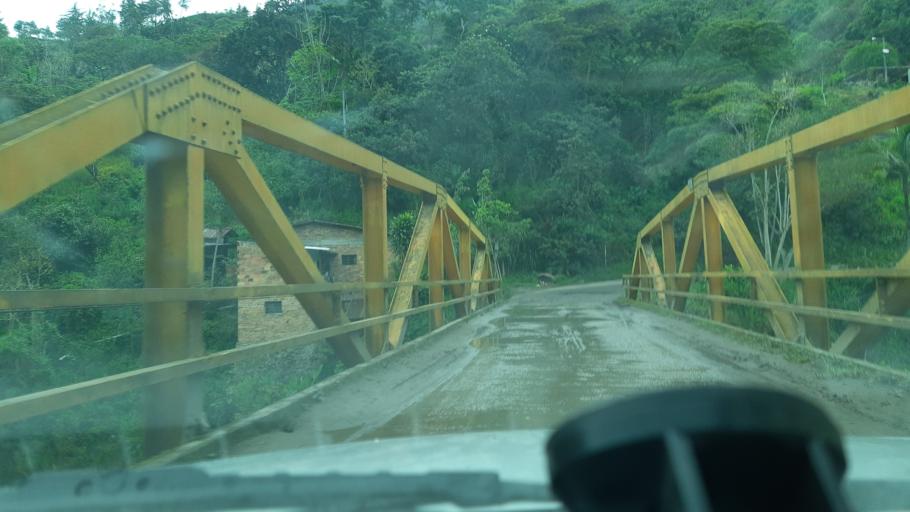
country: CO
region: Boyaca
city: Chinavita
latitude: 5.1858
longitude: -73.3830
